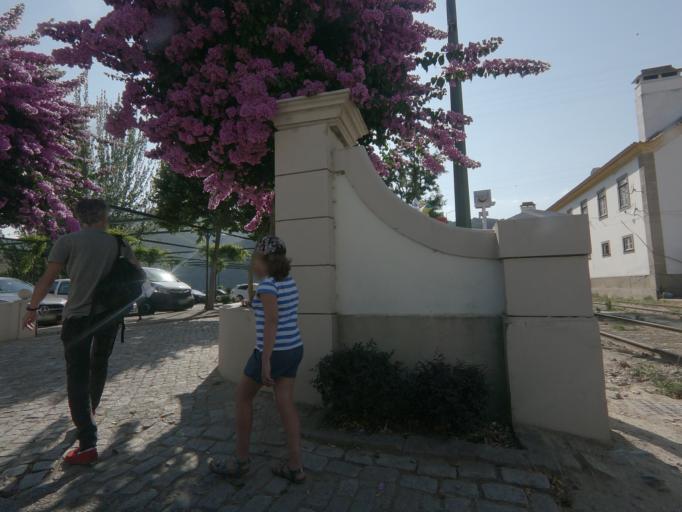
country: PT
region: Vila Real
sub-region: Sabrosa
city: Vilela
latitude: 41.1894
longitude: -7.5421
